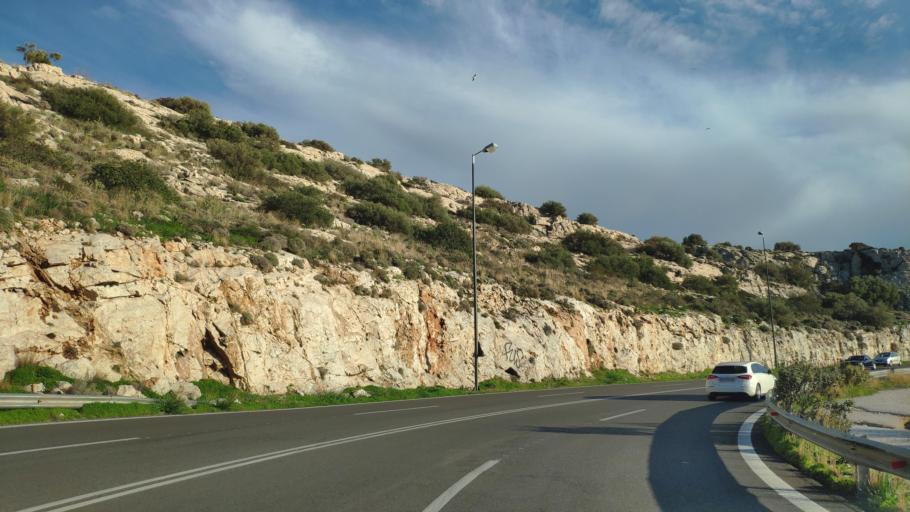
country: GR
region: Attica
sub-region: Nomarchia Anatolikis Attikis
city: Vouliagmeni
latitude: 37.7985
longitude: 23.7911
